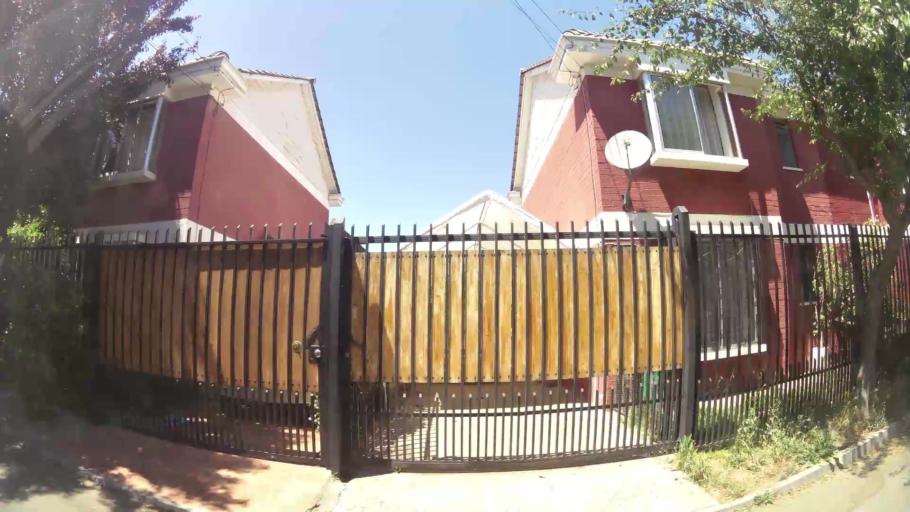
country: CL
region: Santiago Metropolitan
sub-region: Provincia de Maipo
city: San Bernardo
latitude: -33.6239
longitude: -70.7111
